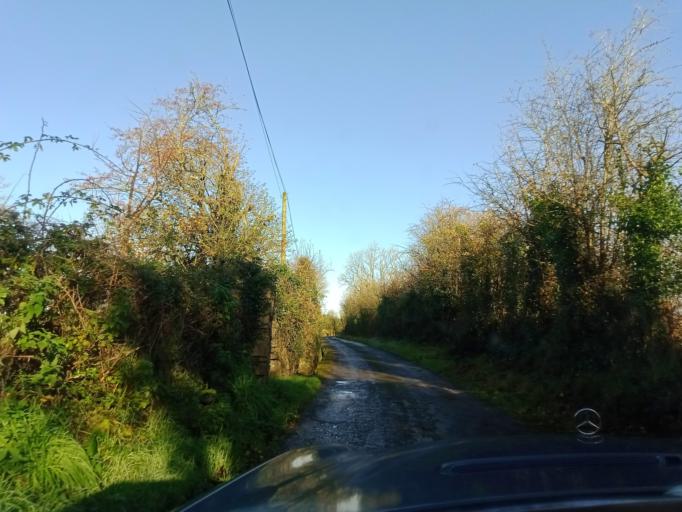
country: IE
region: Leinster
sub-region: Kilkenny
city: Mooncoin
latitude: 52.2904
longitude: -7.2056
